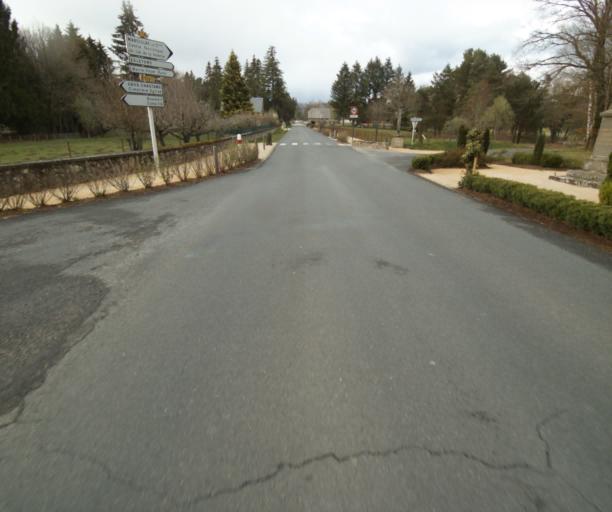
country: FR
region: Limousin
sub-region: Departement de la Correze
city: Saint-Privat
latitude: 45.2131
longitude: 2.0031
